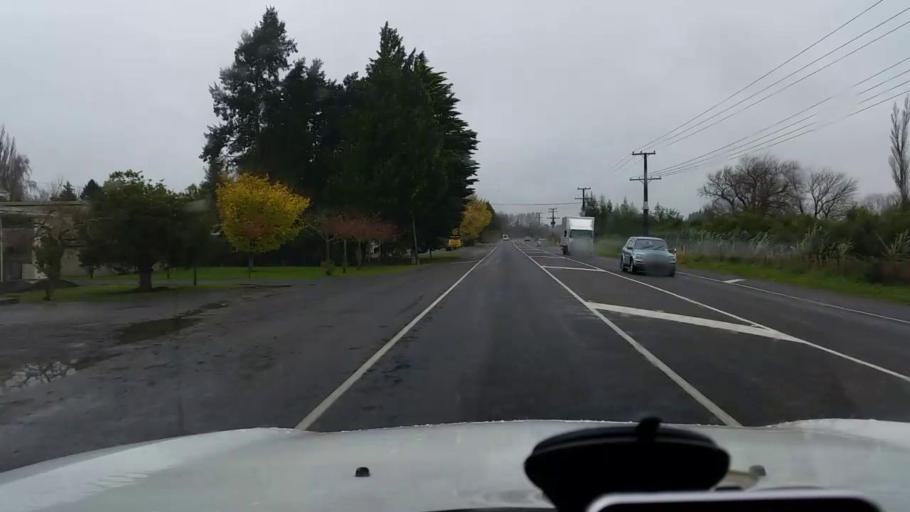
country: NZ
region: Wellington
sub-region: Masterton District
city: Masterton
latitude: -41.0712
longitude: 175.4707
